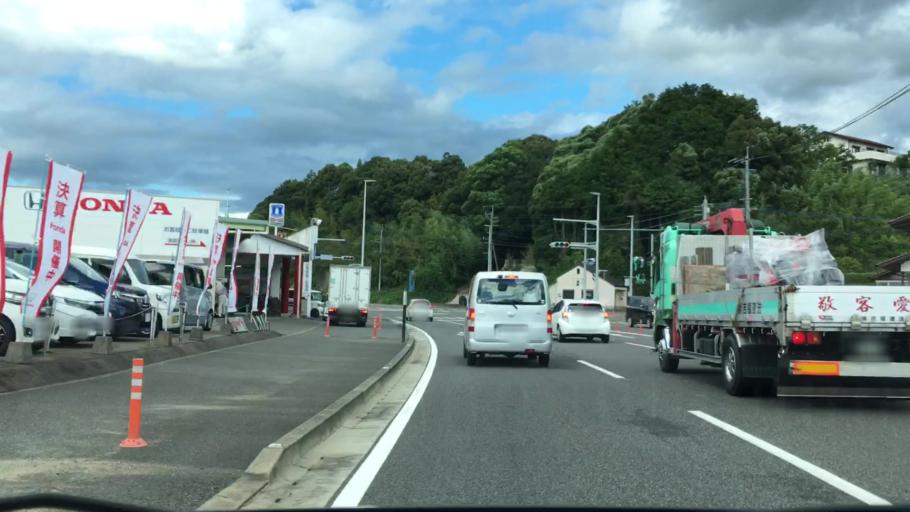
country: JP
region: Saga Prefecture
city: Imaricho-ko
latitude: 33.2767
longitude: 129.8944
